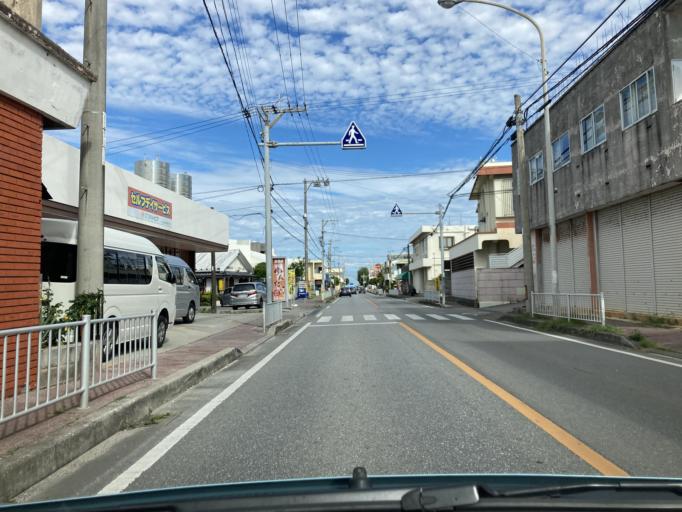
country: JP
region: Okinawa
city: Ishikawa
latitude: 26.4121
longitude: 127.7323
